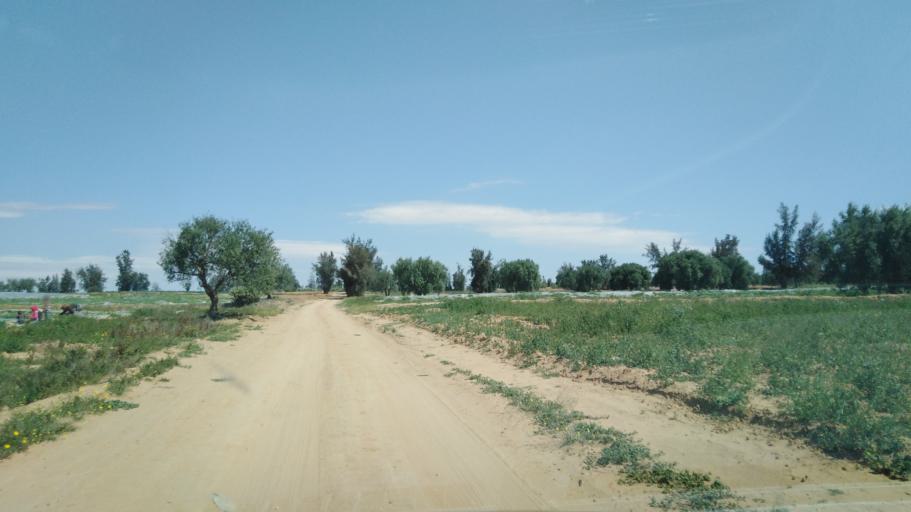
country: TN
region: Safaqis
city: Sfax
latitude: 34.7697
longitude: 10.5277
